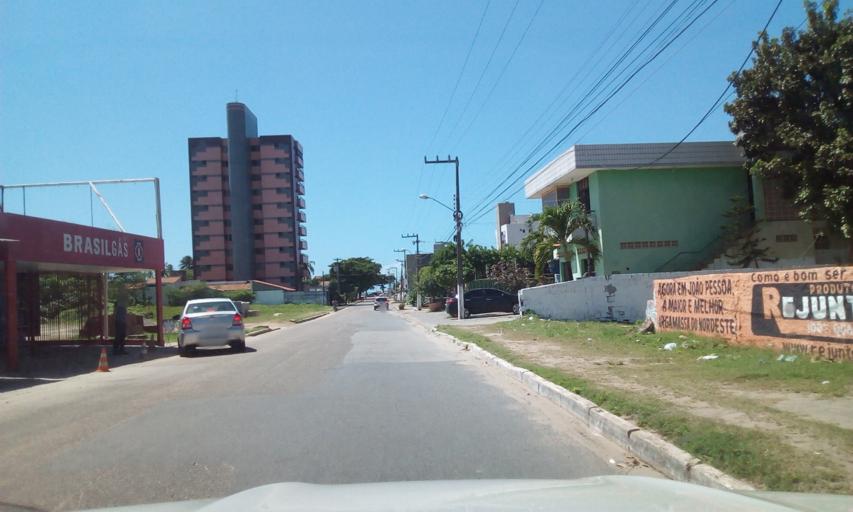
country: BR
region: Paraiba
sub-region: Cabedelo
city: Cabedelo
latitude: -7.0208
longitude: -34.8331
